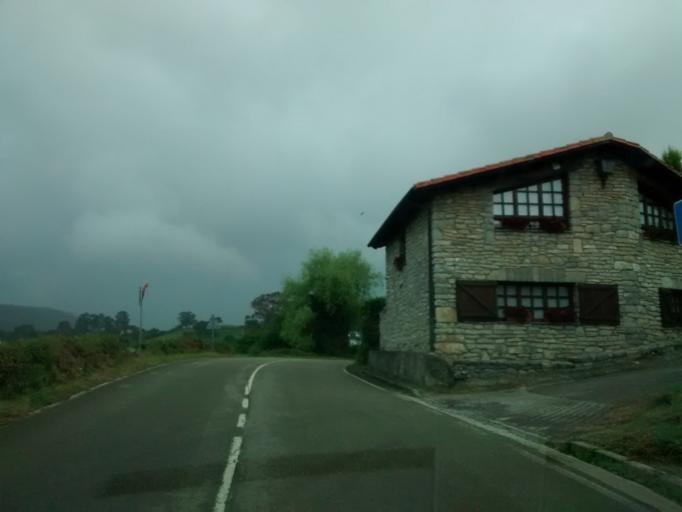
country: ES
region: Asturias
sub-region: Province of Asturias
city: Villaviciosa
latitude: 43.5253
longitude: -5.3736
